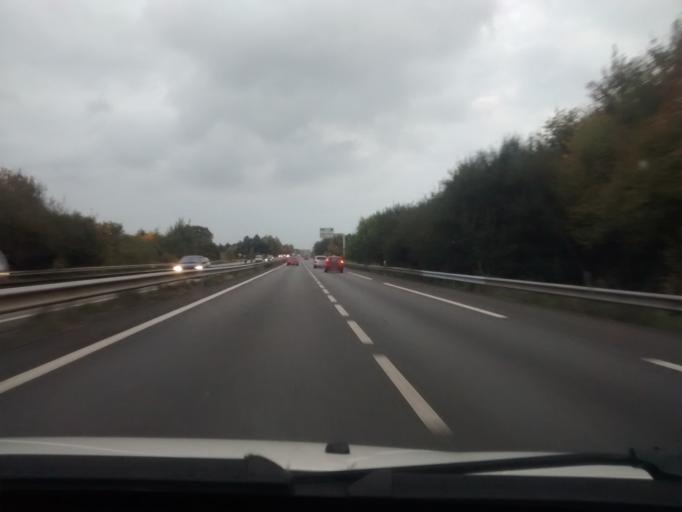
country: FR
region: Brittany
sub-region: Departement d'Ille-et-Vilaine
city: Montgermont
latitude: 48.1584
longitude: -1.7049
